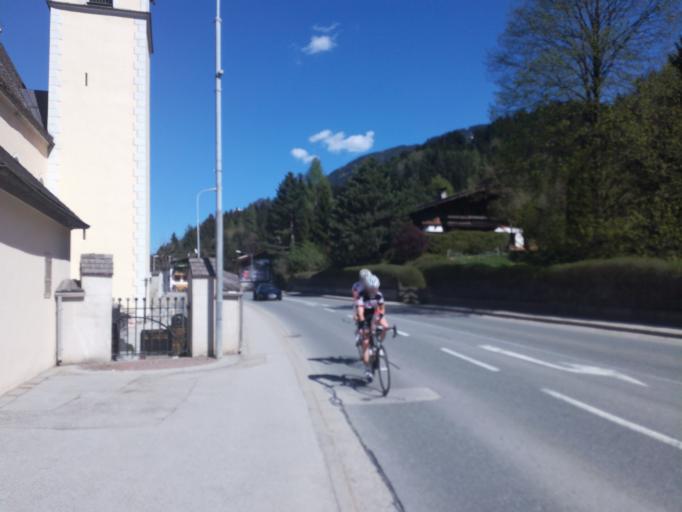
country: AT
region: Tyrol
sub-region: Politischer Bezirk Schwaz
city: Pill
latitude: 47.3201
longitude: 11.6812
